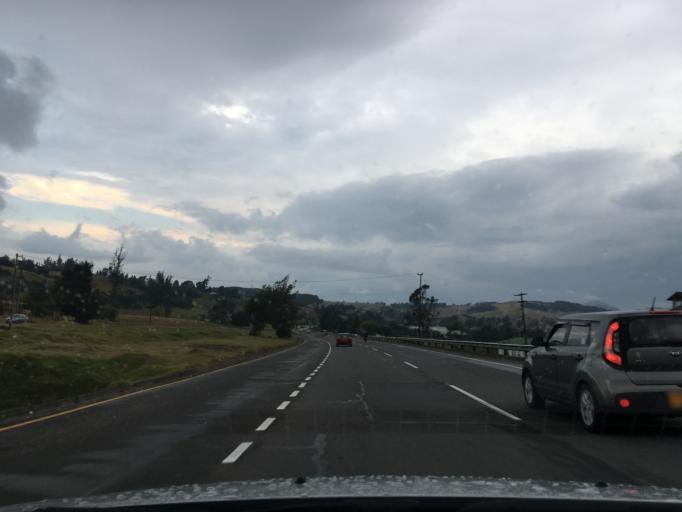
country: CO
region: Cundinamarca
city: Choconta
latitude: 5.1127
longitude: -73.6997
